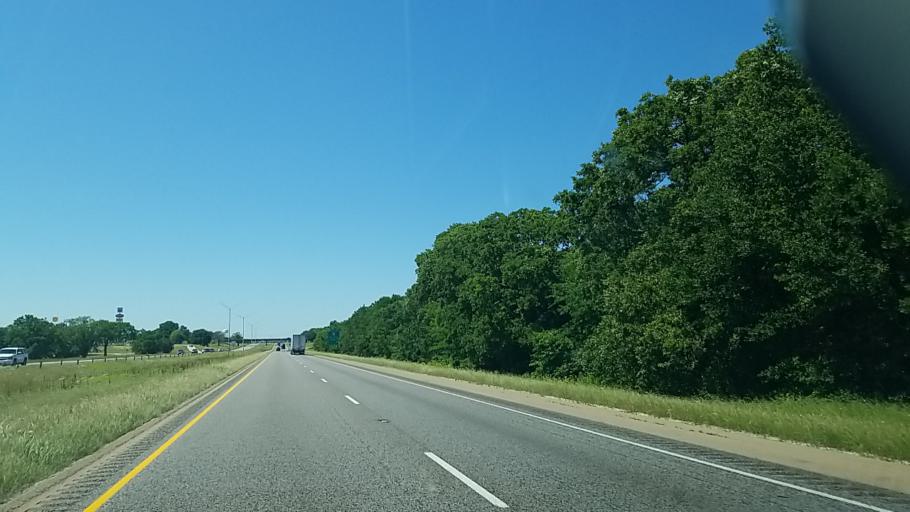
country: US
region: Texas
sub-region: Freestone County
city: Fairfield
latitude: 31.7075
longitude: -96.1742
